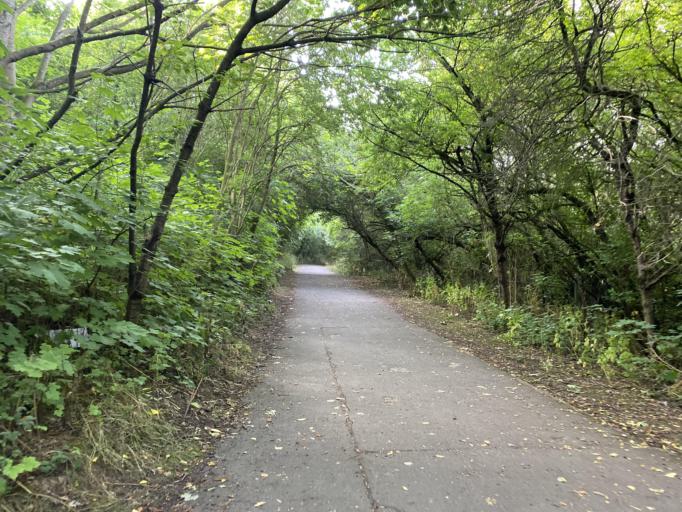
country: GB
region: England
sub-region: Suffolk
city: Haverhill
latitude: 52.0788
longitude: 0.4507
